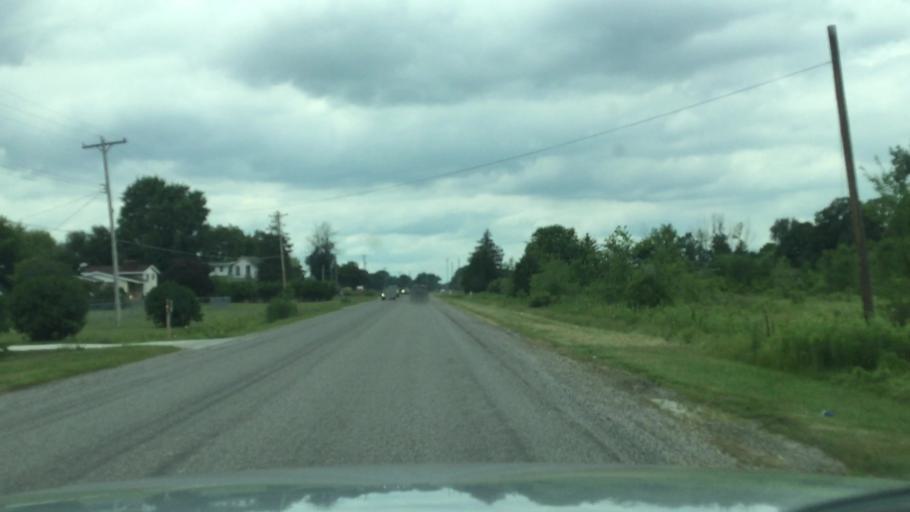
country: US
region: Michigan
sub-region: Saginaw County
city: Birch Run
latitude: 43.2502
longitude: -83.8115
